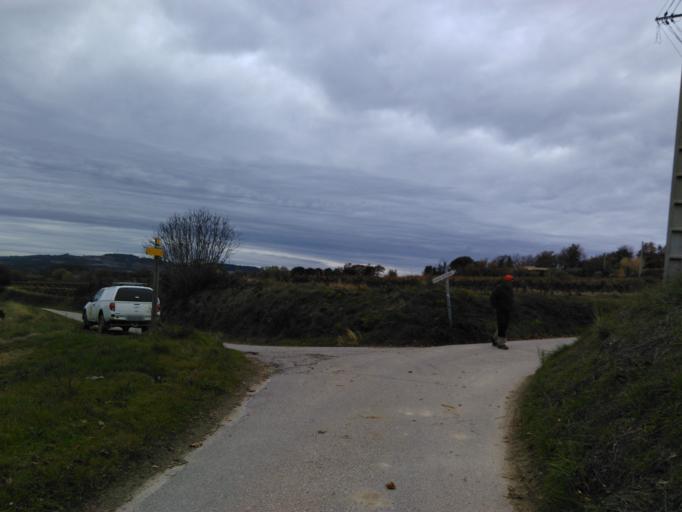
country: FR
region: Rhone-Alpes
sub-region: Departement de la Drome
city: Mirabel-aux-Baronnies
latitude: 44.2619
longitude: 5.1438
